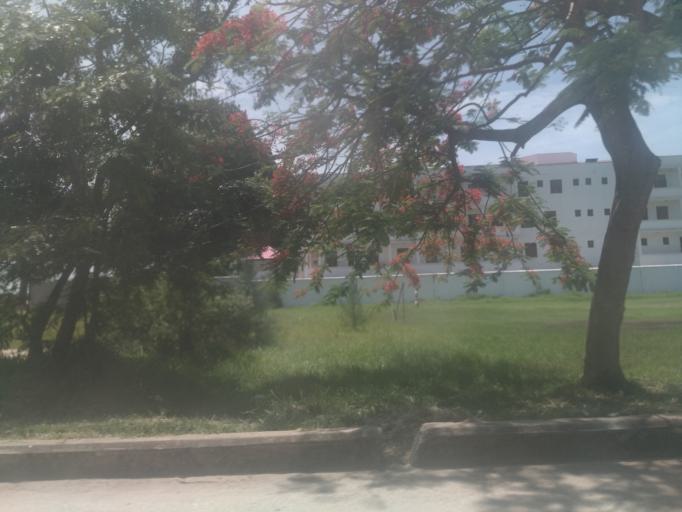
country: TZ
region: Zanzibar Urban/West
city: Zanzibar
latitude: -6.1696
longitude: 39.1919
